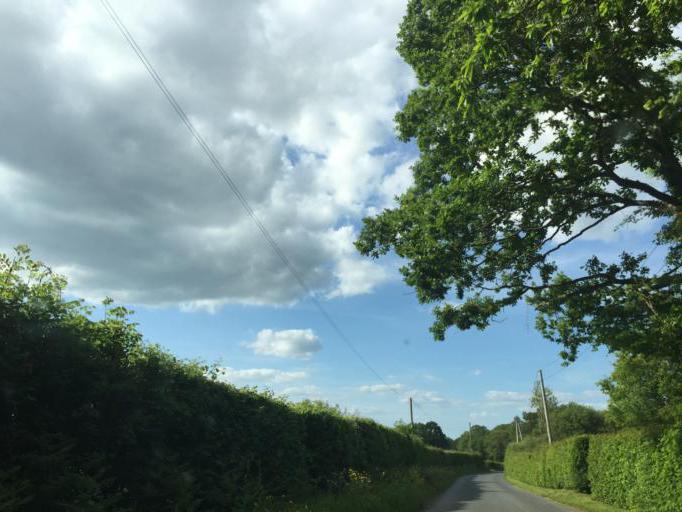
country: GB
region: England
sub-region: East Sussex
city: Wadhurst
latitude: 51.0341
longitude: 0.2825
